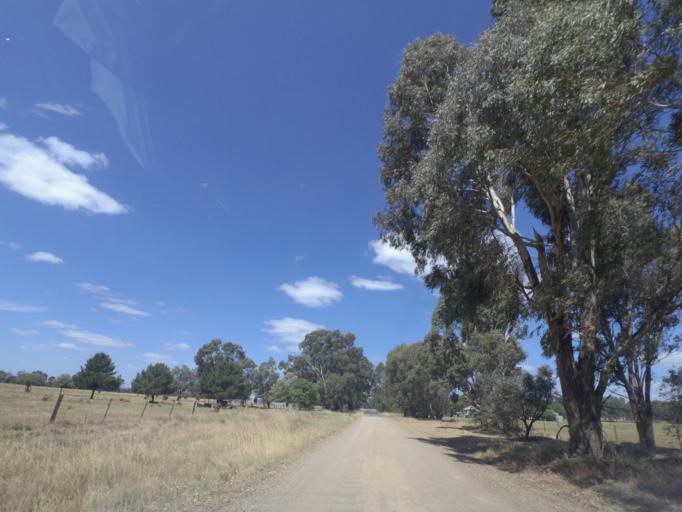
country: AU
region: Victoria
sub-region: Wangaratta
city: Wangaratta
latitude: -36.4001
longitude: 146.2948
